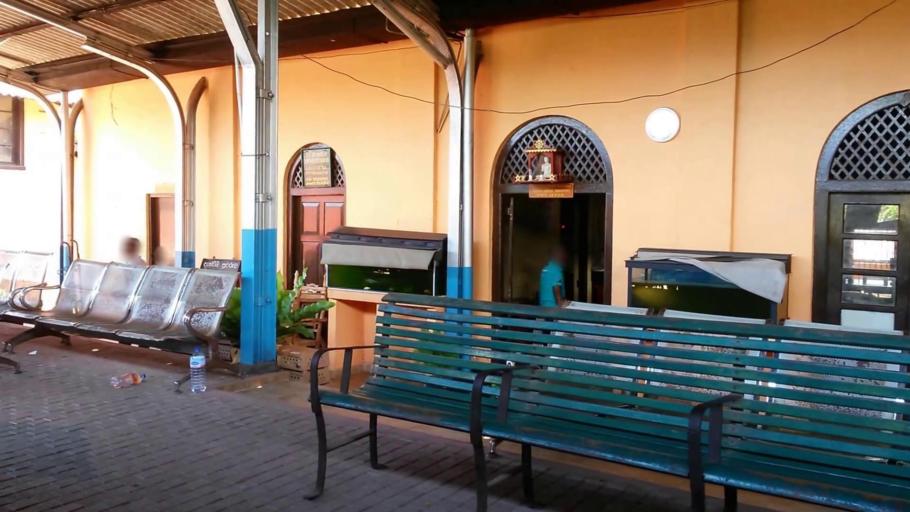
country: LK
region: Southern
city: Hikkaduwa
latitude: 6.1441
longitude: 80.1001
